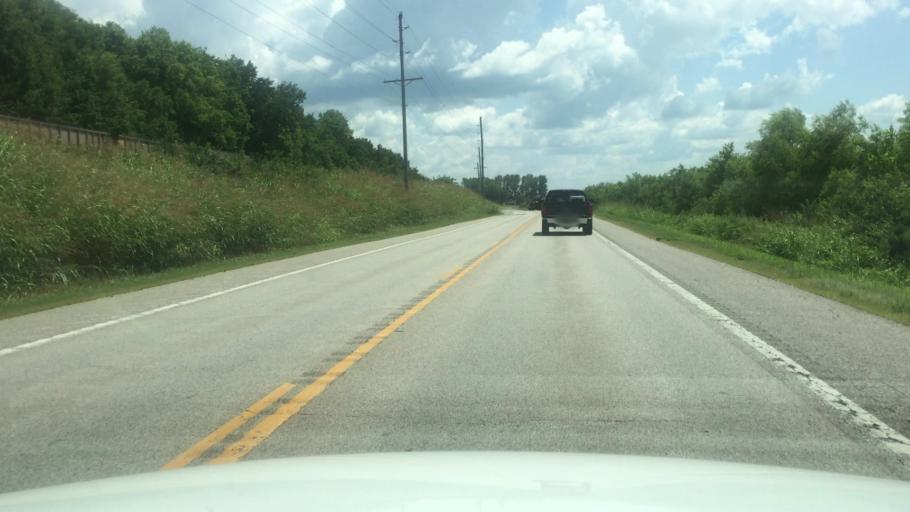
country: US
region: Kansas
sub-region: Atchison County
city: Atchison
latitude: 39.5368
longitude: -95.0398
